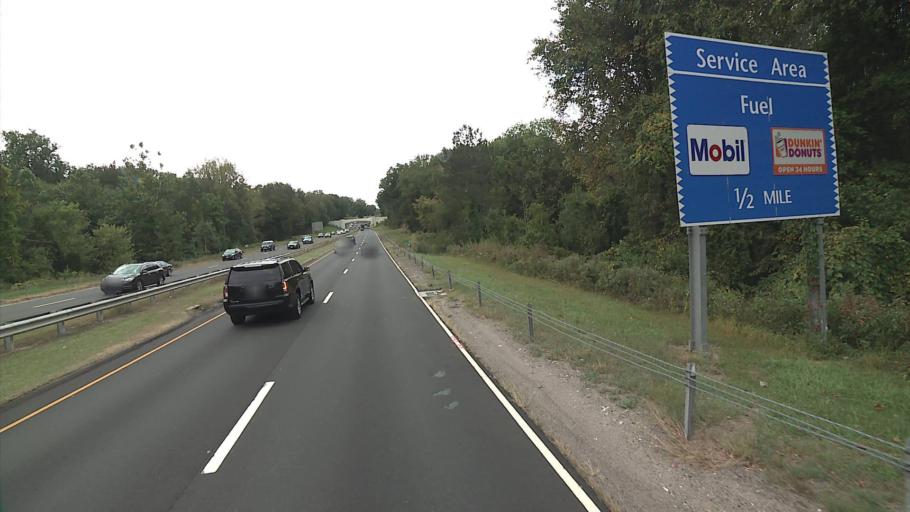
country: US
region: Connecticut
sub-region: Fairfield County
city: New Canaan
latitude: 41.1252
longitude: -73.4706
